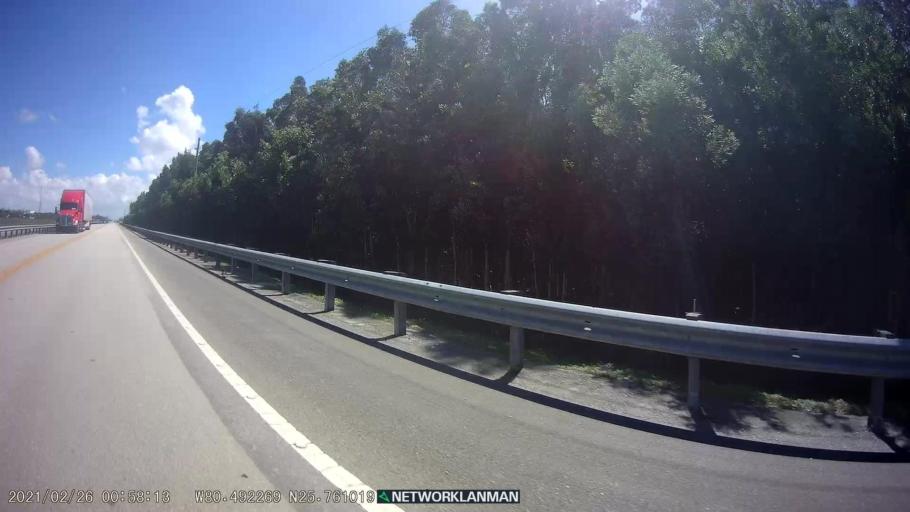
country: US
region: Florida
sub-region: Miami-Dade County
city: Kendall West
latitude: 25.7606
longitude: -80.4918
